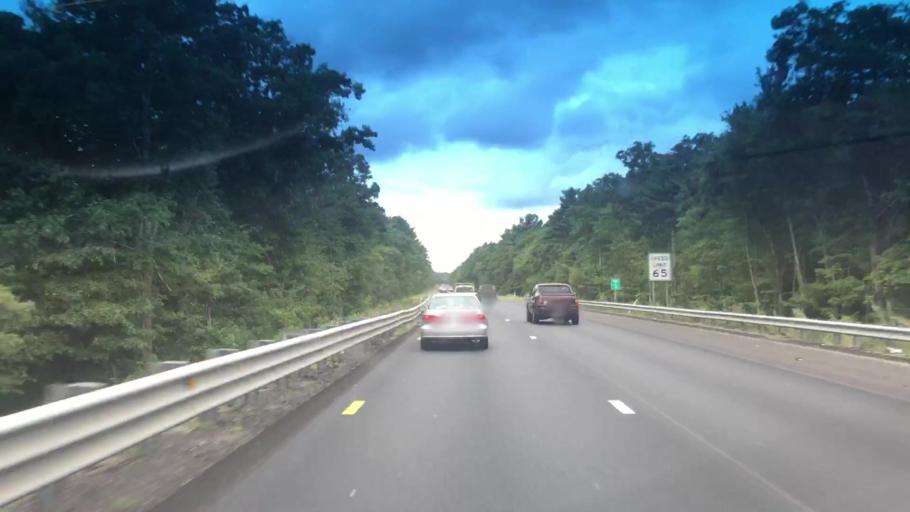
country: US
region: Massachusetts
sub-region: Plymouth County
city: West Wareham
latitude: 41.8003
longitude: -70.7635
